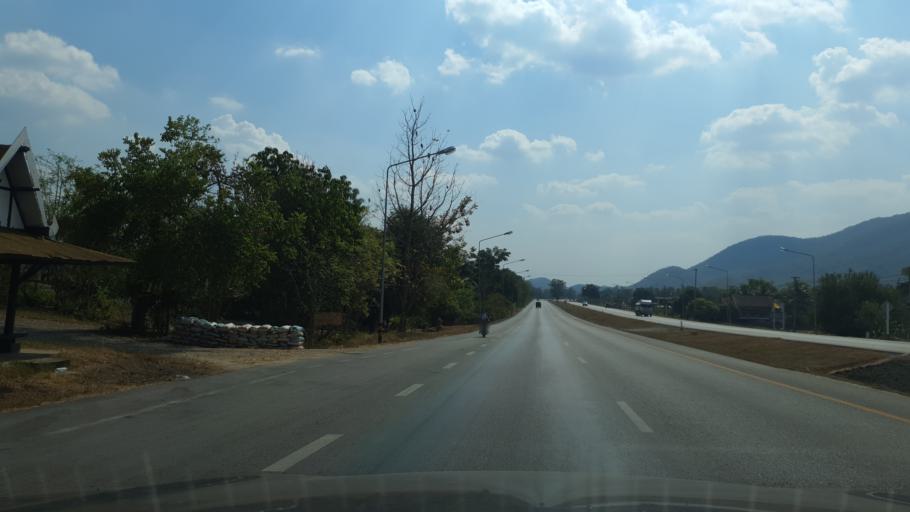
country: TH
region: Lampang
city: Mae Phrik
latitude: 17.3607
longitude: 99.1476
